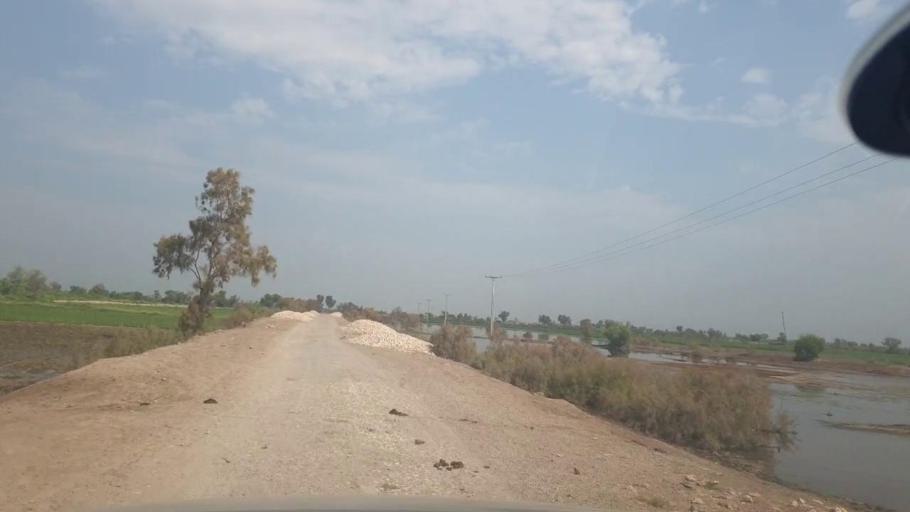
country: PK
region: Balochistan
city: Mehrabpur
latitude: 28.0684
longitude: 68.1028
